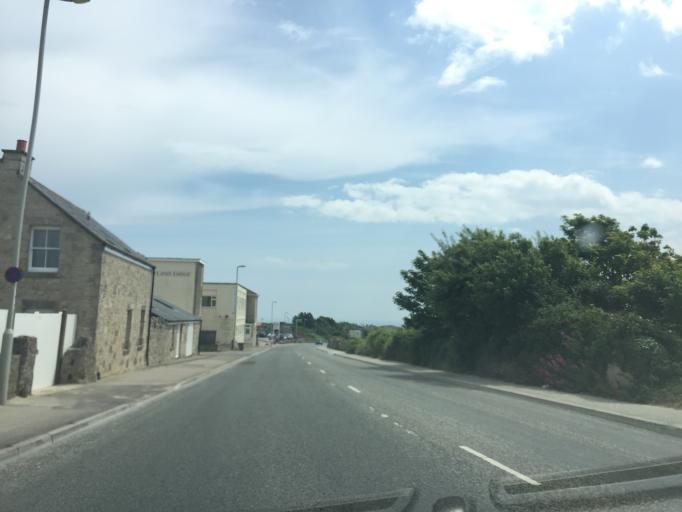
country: GB
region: England
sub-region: Dorset
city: Fortuneswell
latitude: 50.5538
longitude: -2.4387
